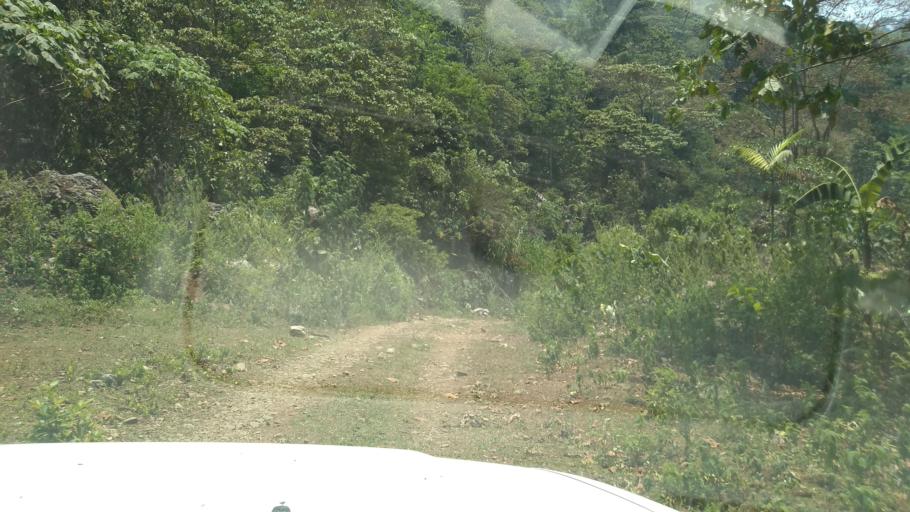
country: MX
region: Veracruz
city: Motzorongo
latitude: 18.6078
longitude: -96.7610
